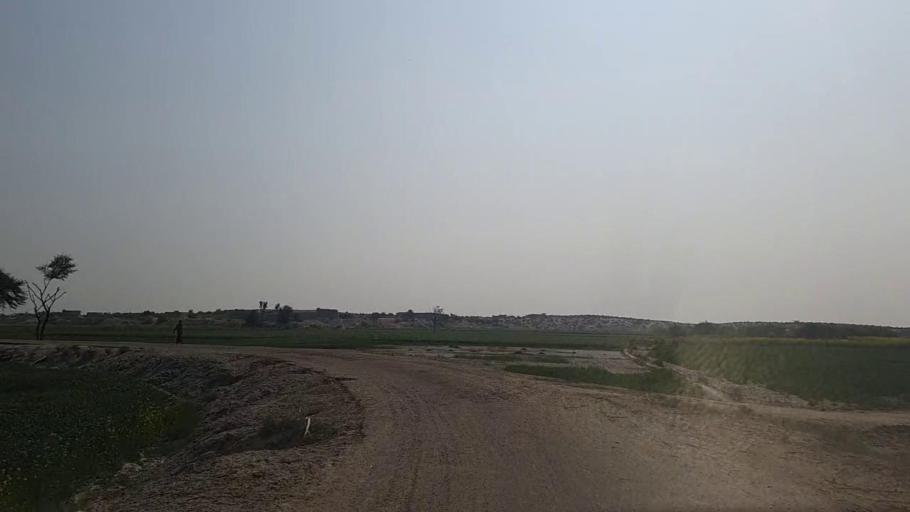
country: PK
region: Sindh
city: Jam Sahib
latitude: 26.4387
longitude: 68.5232
